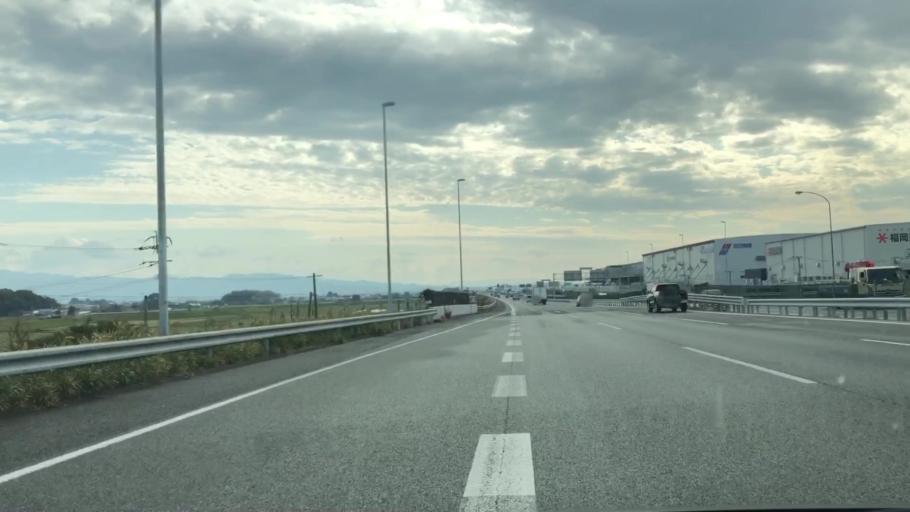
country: JP
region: Saga Prefecture
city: Tosu
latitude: 33.3926
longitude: 130.5384
